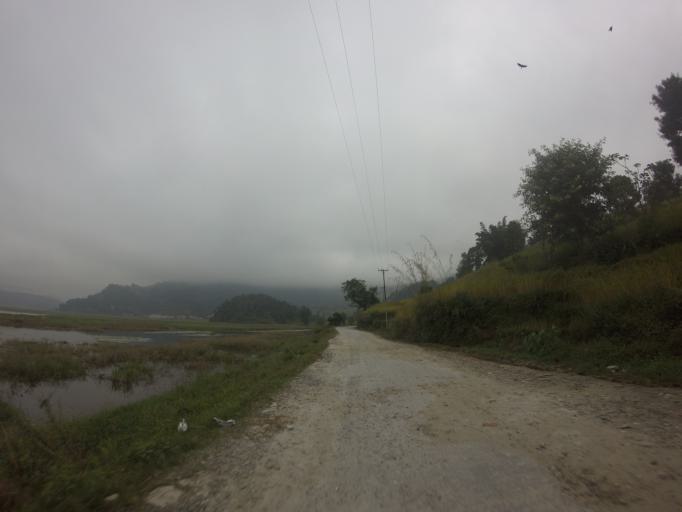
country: NP
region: Western Region
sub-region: Gandaki Zone
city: Pokhara
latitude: 28.2288
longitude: 83.9324
